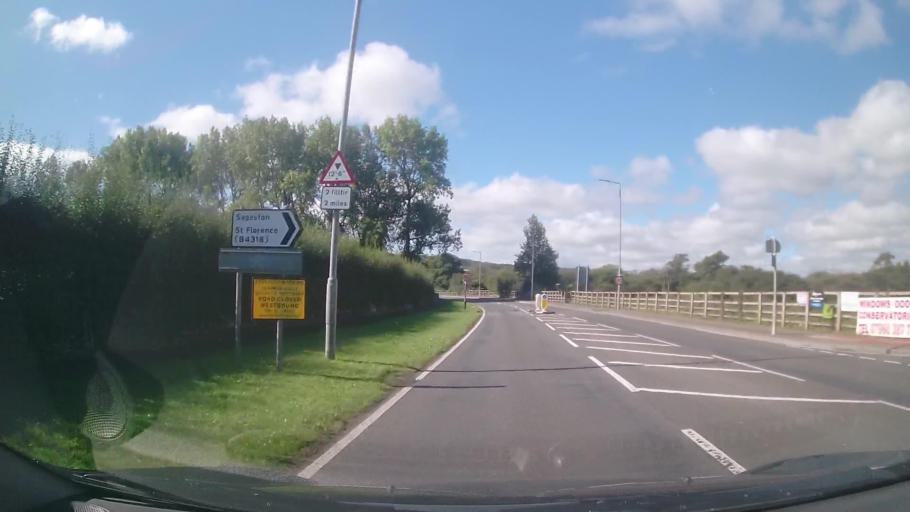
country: GB
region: Wales
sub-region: Pembrokeshire
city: Penally
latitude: 51.6710
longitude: -4.7213
